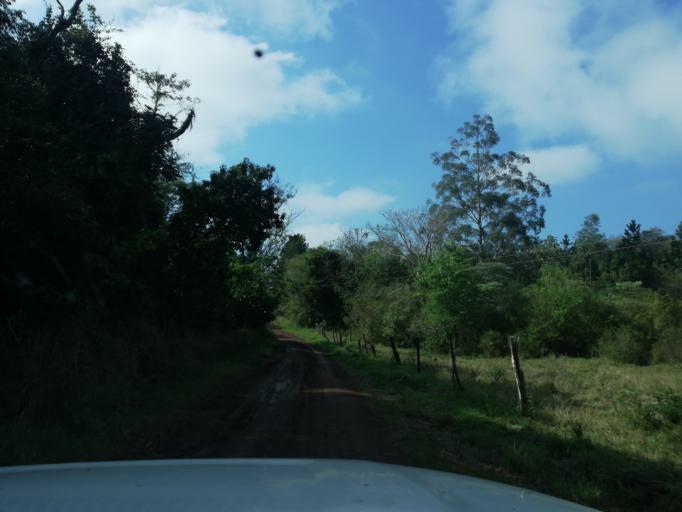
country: AR
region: Misiones
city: Cerro Azul
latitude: -27.6129
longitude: -55.5297
